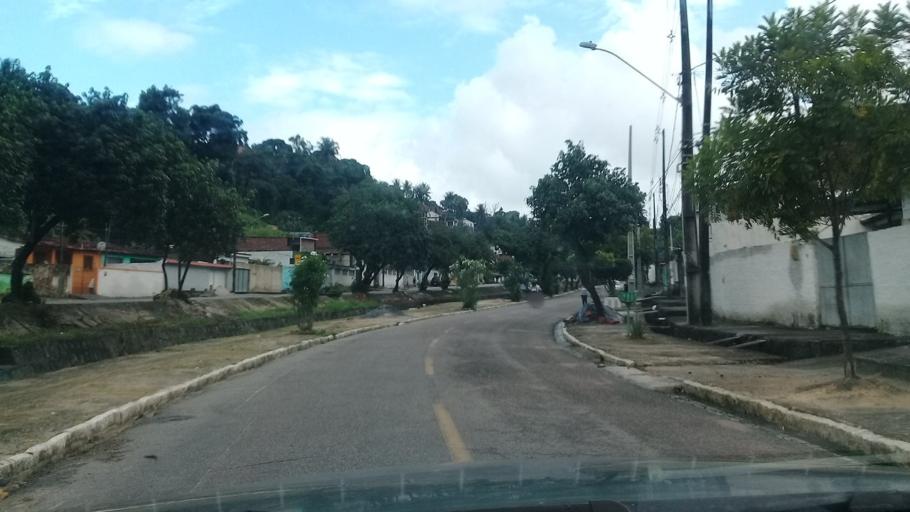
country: BR
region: Pernambuco
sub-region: Jaboatao Dos Guararapes
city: Jaboatao dos Guararapes
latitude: -8.1186
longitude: -34.9513
